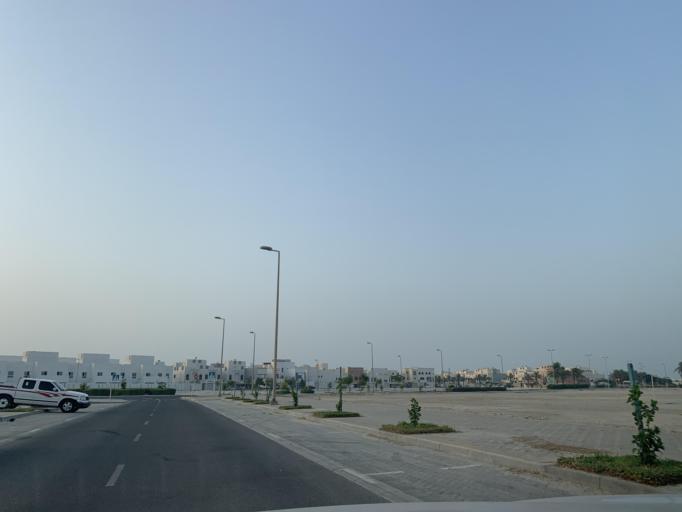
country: BH
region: Manama
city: Jidd Hafs
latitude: 26.2230
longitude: 50.4397
